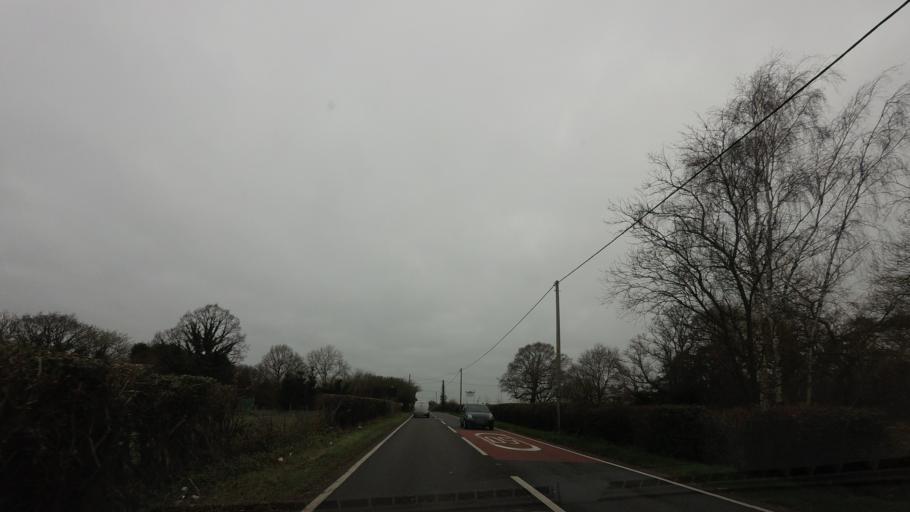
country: GB
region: England
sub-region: East Sussex
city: Saint Leonards-on-Sea
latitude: 50.9092
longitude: 0.5461
